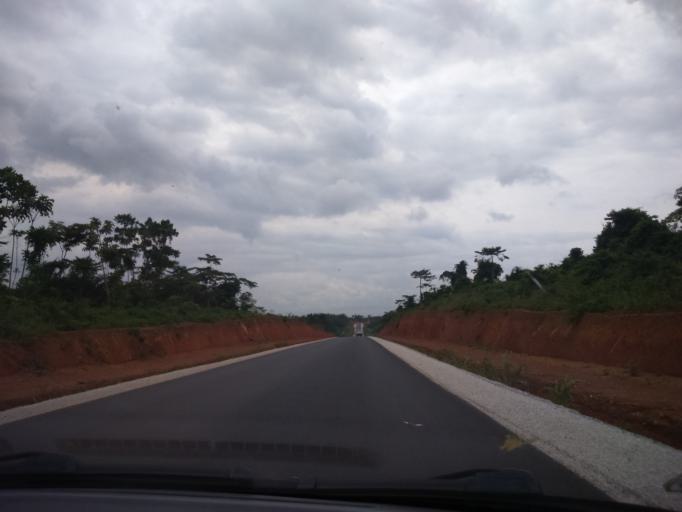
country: CI
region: Lagunes
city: Akoupe
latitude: 6.3263
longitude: -3.8386
